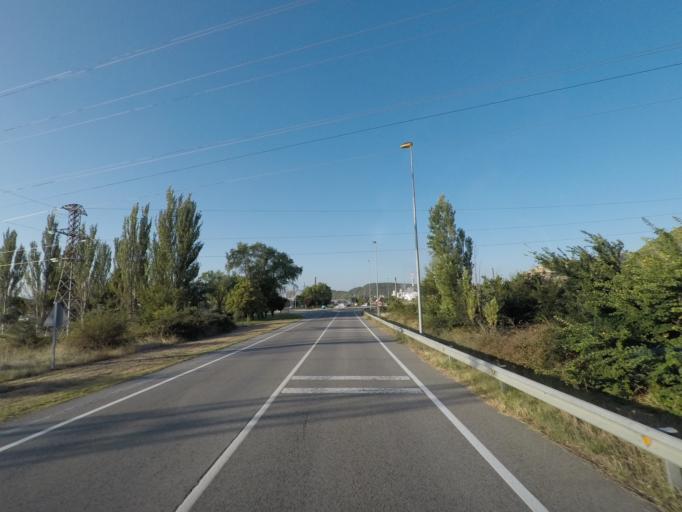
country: ES
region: Navarre
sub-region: Provincia de Navarra
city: Liedena
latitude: 42.5981
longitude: -1.2773
